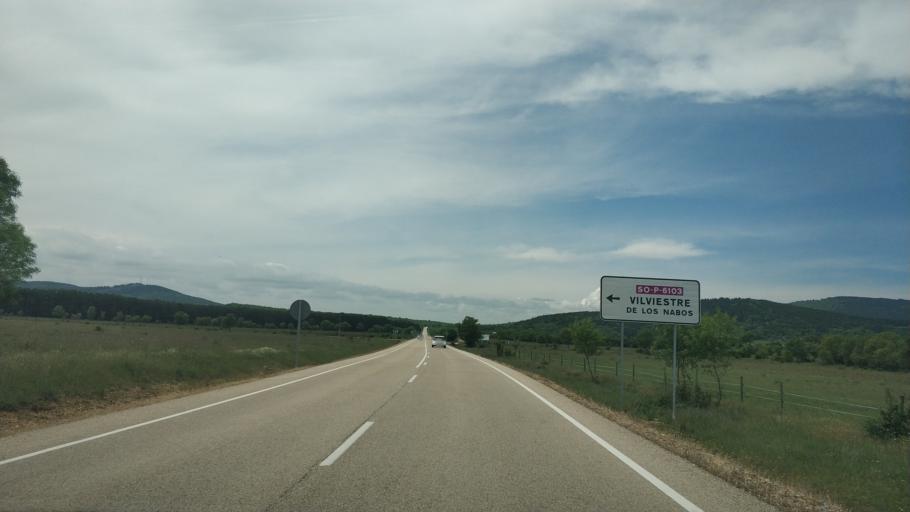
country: ES
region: Castille and Leon
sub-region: Provincia de Soria
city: Sotillo del Rincon
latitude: 41.8960
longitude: -2.6652
